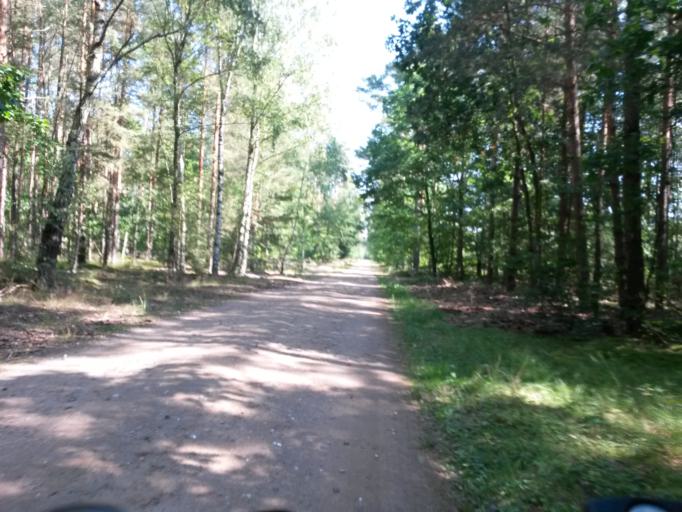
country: DE
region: Brandenburg
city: Zehdenick
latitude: 53.0363
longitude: 13.3987
